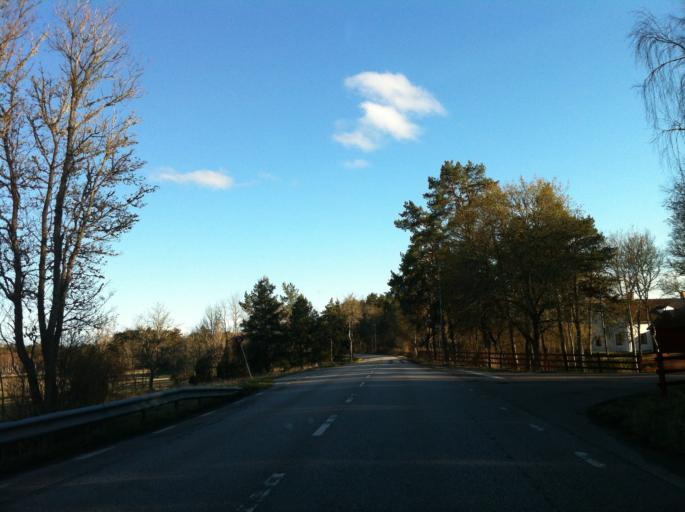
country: SE
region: Uppsala
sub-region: Osthammars Kommun
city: Anneberg
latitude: 60.1827
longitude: 18.3984
